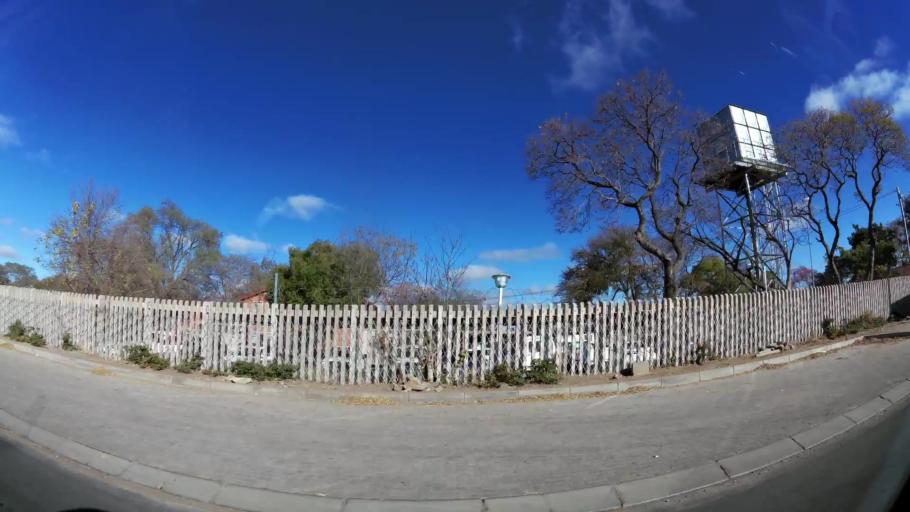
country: ZA
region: Limpopo
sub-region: Capricorn District Municipality
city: Polokwane
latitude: -23.8977
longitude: 29.4536
